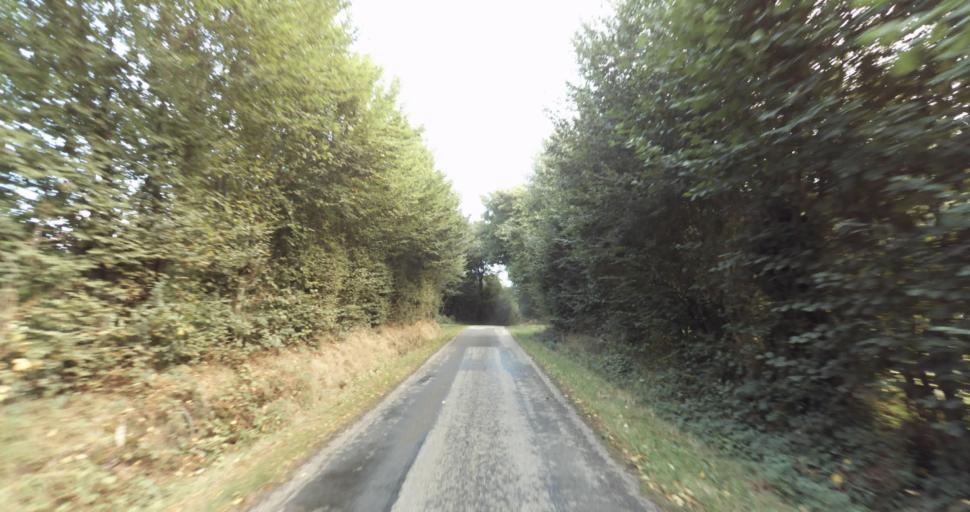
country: FR
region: Lower Normandy
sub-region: Departement de l'Orne
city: Gace
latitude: 48.7566
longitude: 0.3570
